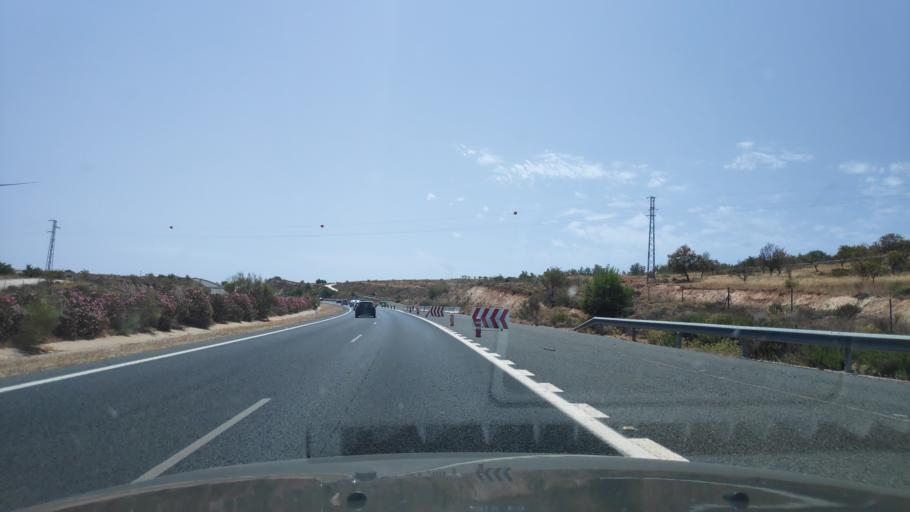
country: ES
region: Andalusia
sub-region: Provincia de Granada
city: Padul
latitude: 37.0070
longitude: -3.6390
